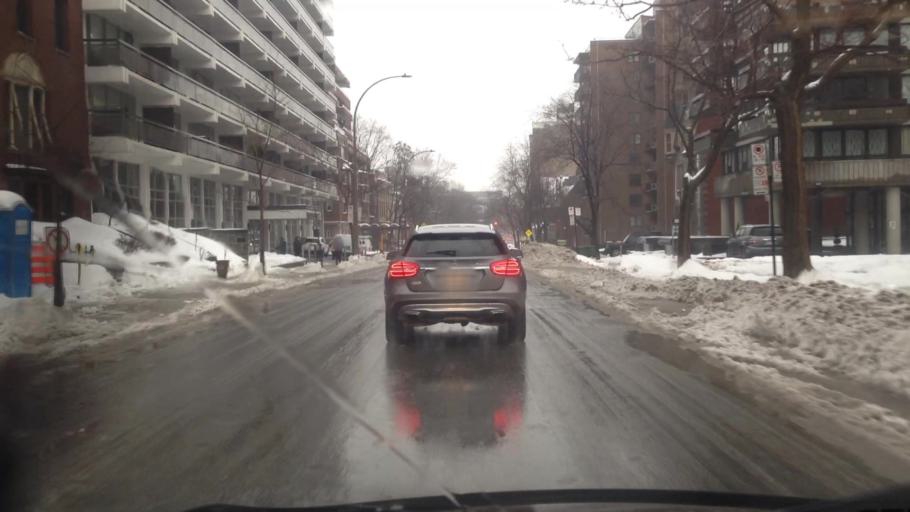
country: CA
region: Quebec
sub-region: Montreal
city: Montreal
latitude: 45.4971
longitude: -73.5861
